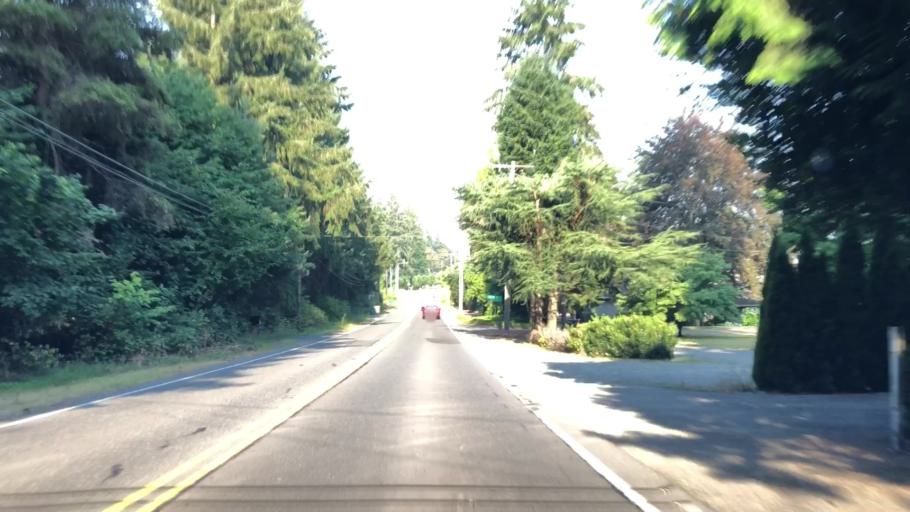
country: US
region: Washington
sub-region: King County
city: Sammamish
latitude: 47.6754
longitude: -122.0737
